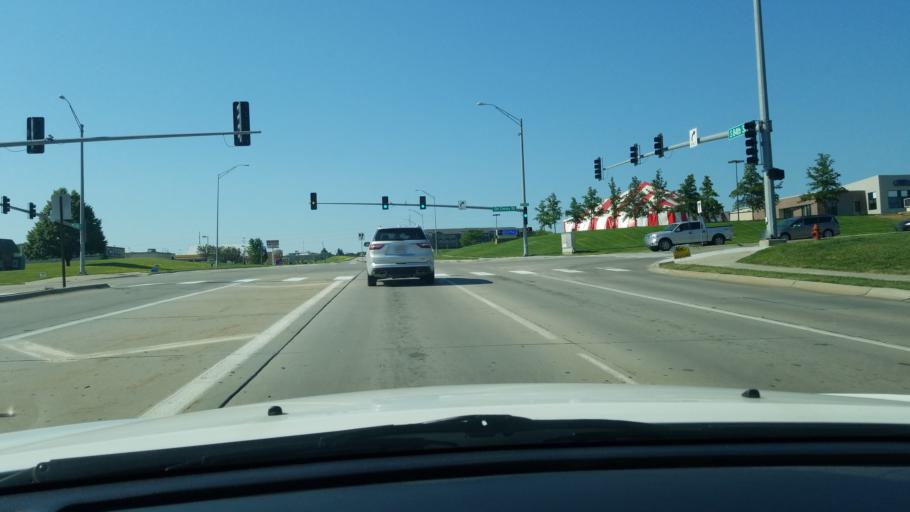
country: US
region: Nebraska
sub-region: Lancaster County
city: Lincoln
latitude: 40.7557
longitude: -96.6062
